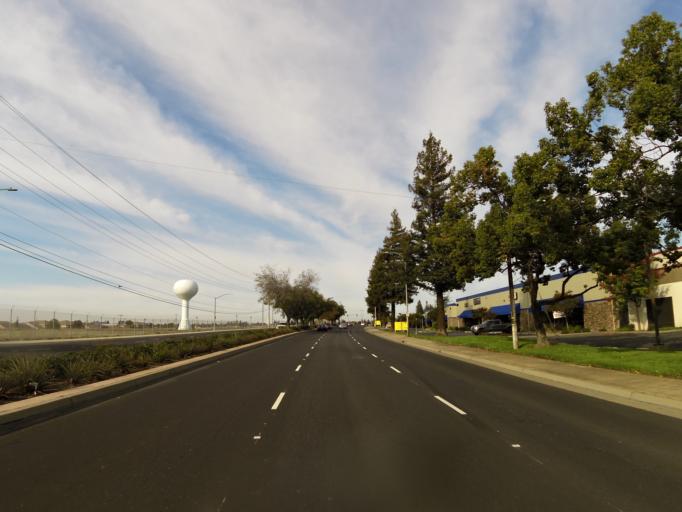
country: US
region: California
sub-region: Sacramento County
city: Rancho Cordova
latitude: 38.5813
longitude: -121.2640
